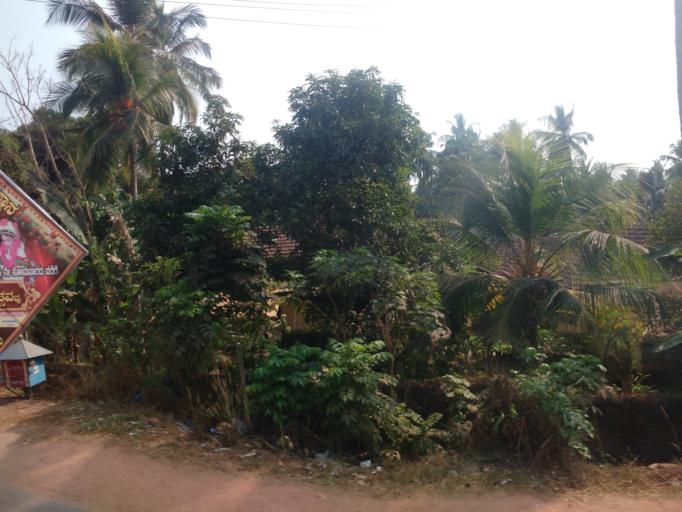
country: IN
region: Karnataka
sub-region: Dakshina Kannada
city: Mangalore
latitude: 12.8702
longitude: 74.8772
